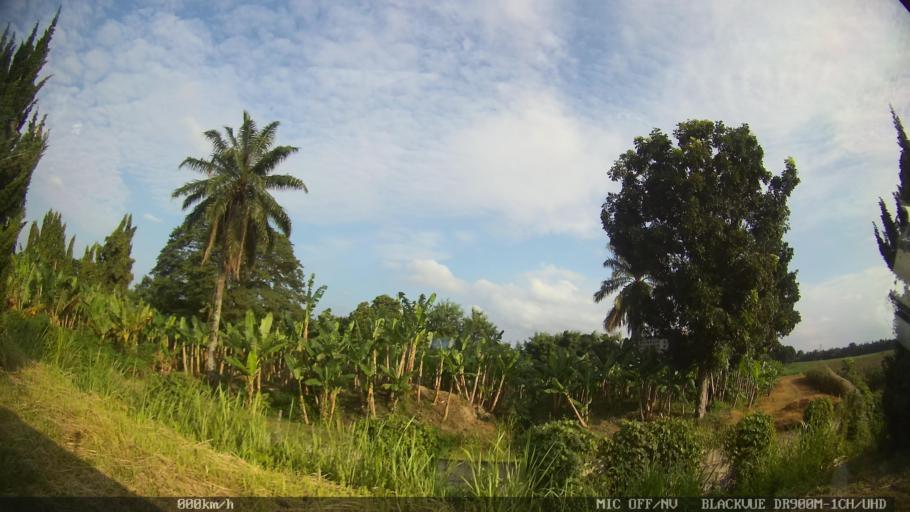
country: ID
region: North Sumatra
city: Sunggal
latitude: 3.6297
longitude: 98.6325
